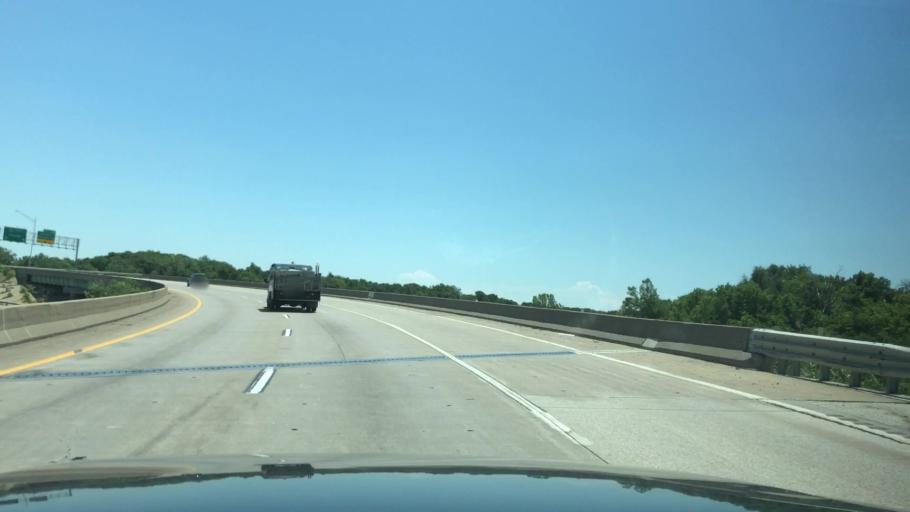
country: US
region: Missouri
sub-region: Saint Louis County
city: Bridgeton
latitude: 38.7705
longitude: -90.4078
